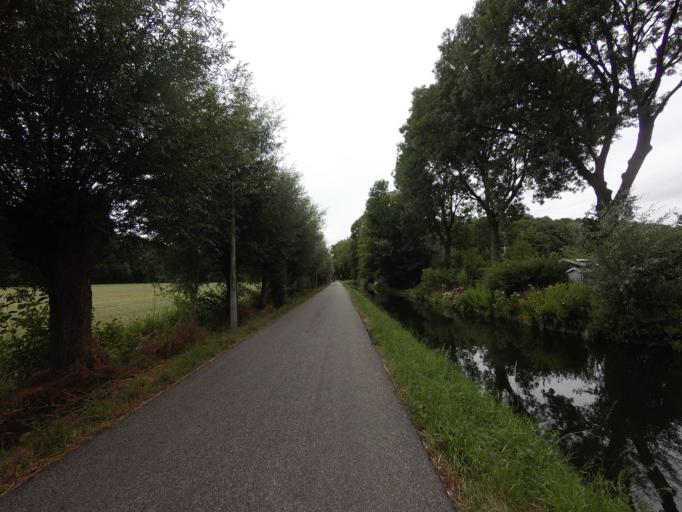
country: NL
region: Utrecht
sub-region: Stichtse Vecht
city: Maarssen
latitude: 52.1243
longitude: 5.0808
